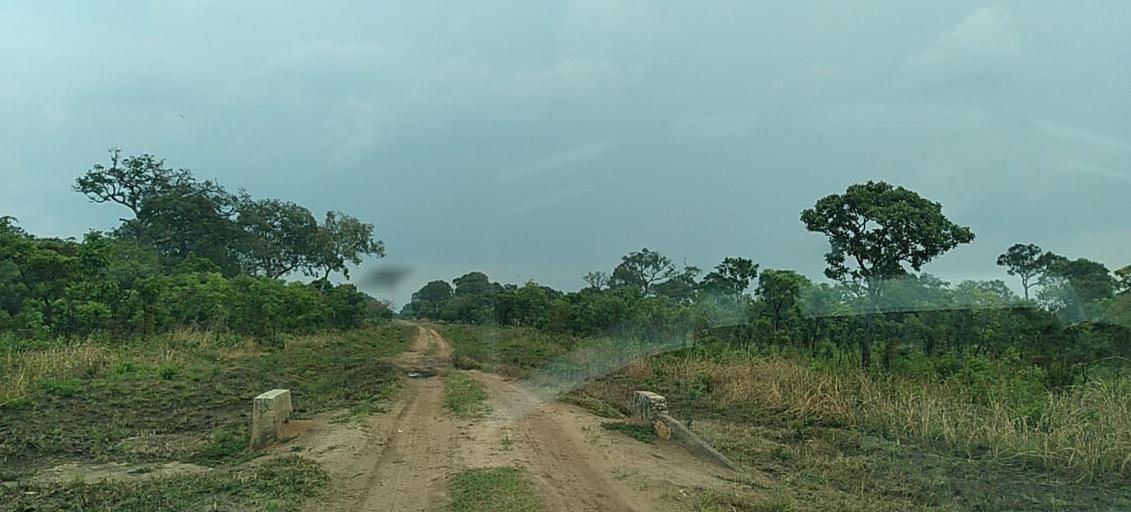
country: ZM
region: North-Western
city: Mwinilunga
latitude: -11.4456
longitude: 24.5909
